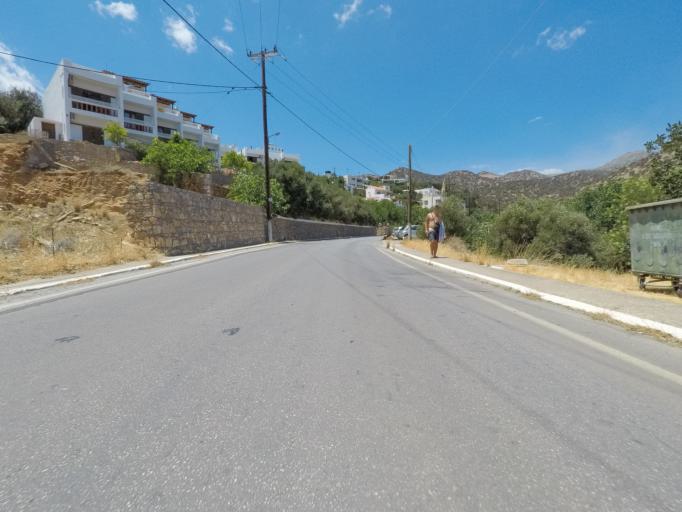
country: GR
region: Crete
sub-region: Nomos Lasithiou
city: Agios Nikolaos
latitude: 35.2172
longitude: 25.7112
